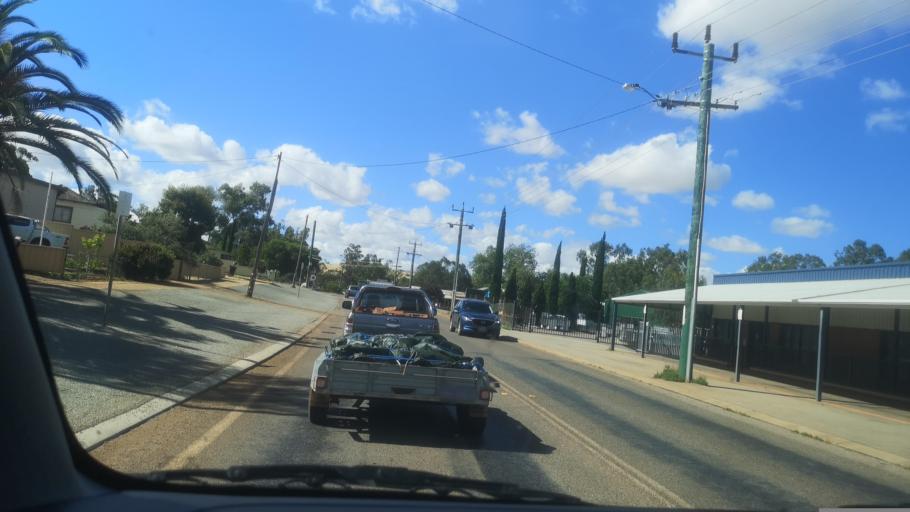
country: AU
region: Western Australia
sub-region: Toodyay
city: Toodyay
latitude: -31.5575
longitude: 116.4761
